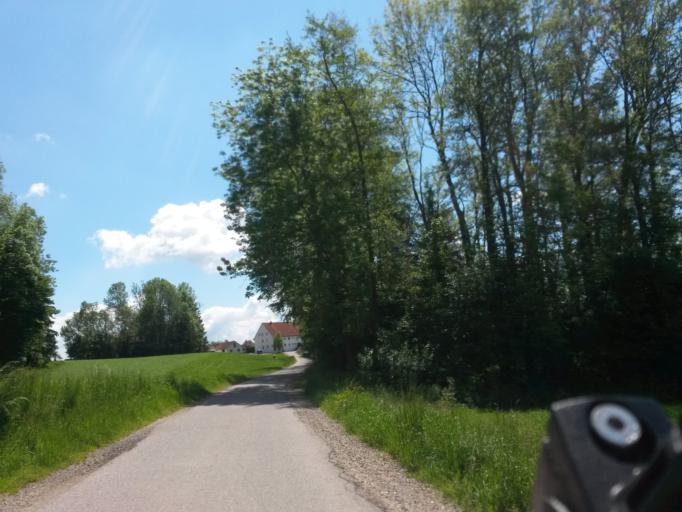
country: DE
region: Baden-Wuerttemberg
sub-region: Tuebingen Region
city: Bad Schussenried
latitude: 48.0137
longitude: 9.6848
